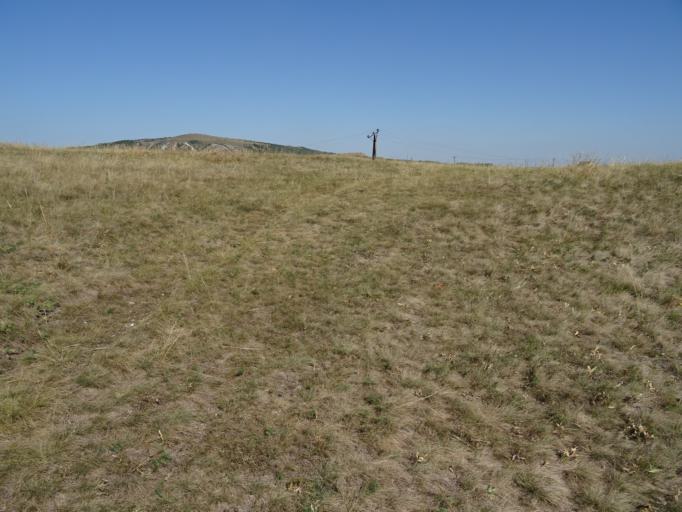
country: HU
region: Veszprem
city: Varpalota
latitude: 47.2061
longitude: 18.1761
